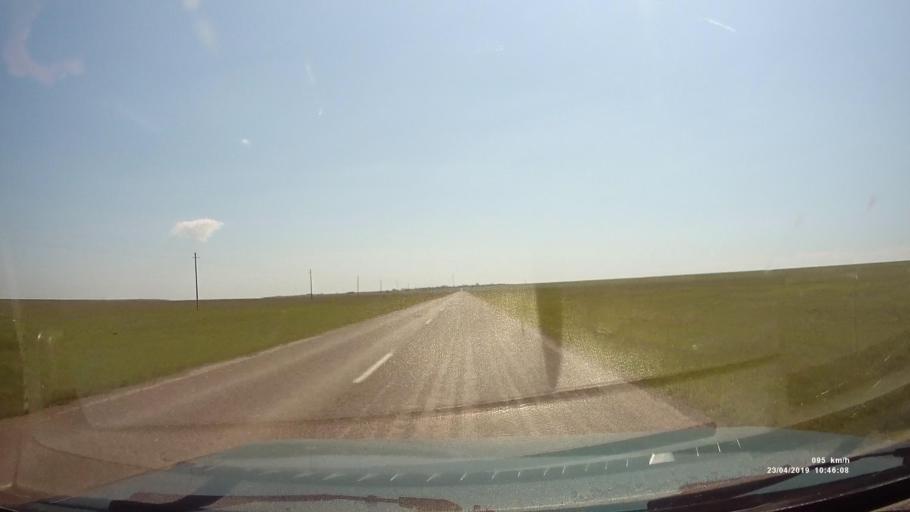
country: RU
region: Kalmykiya
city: Yashalta
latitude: 46.4455
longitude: 42.6860
